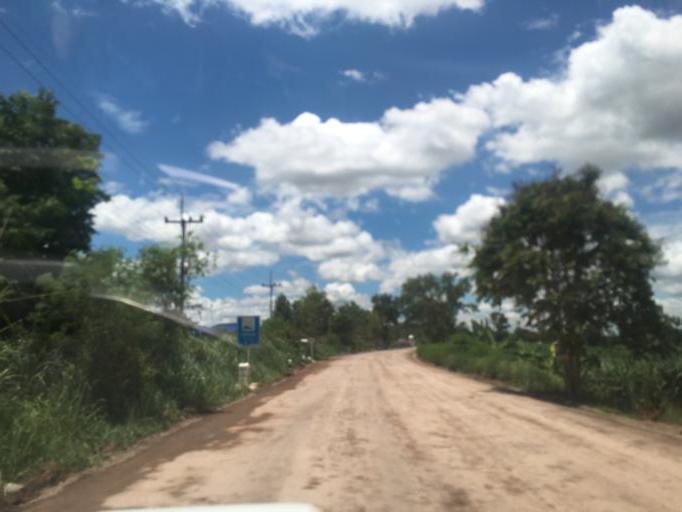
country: TH
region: Changwat Udon Thani
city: Nong Saeng
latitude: 17.1836
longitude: 102.7697
